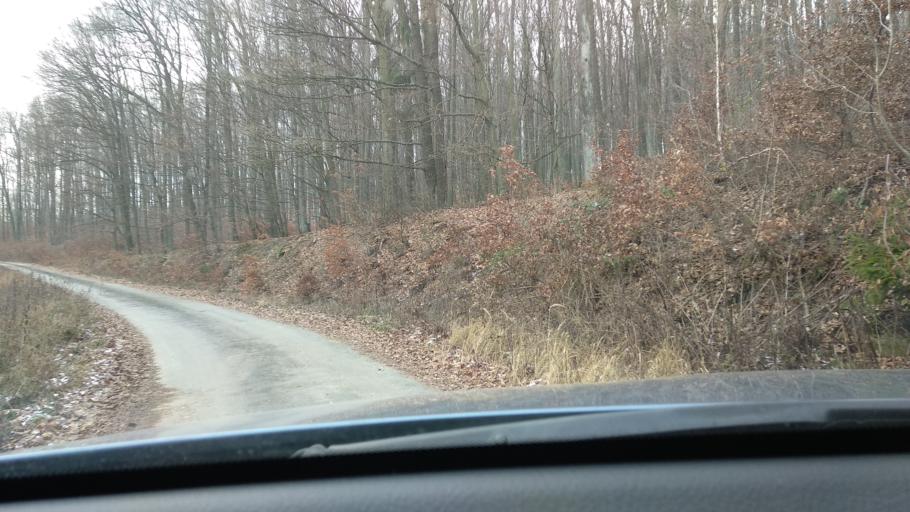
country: SK
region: Trenciansky
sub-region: Okres Trencin
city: Trencin
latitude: 48.8016
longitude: 18.0828
